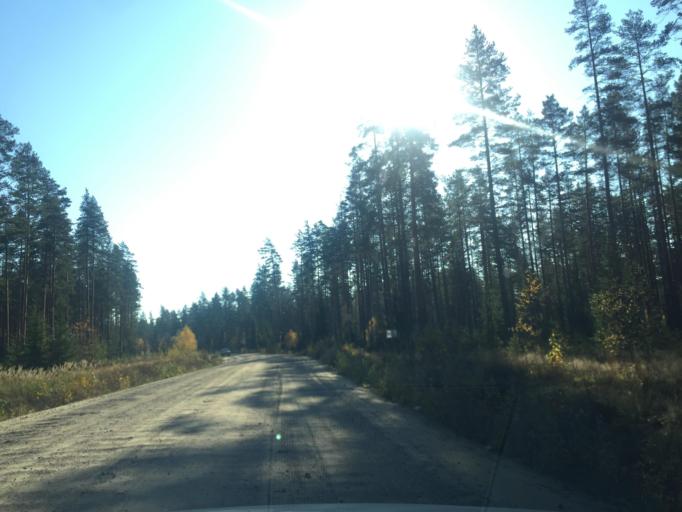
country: RU
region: Republic of Karelia
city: Lakhdenpokh'ya
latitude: 61.3853
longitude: 29.9618
